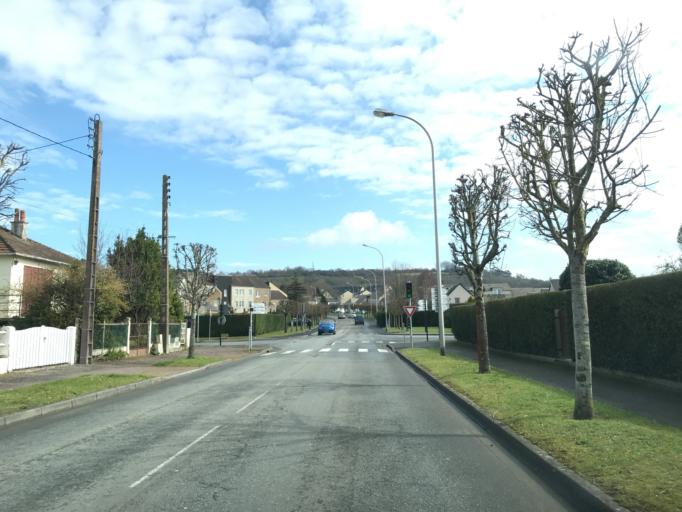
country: FR
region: Lower Normandy
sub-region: Departement du Calvados
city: Dives-sur-Mer
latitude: 49.2833
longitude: -0.0981
